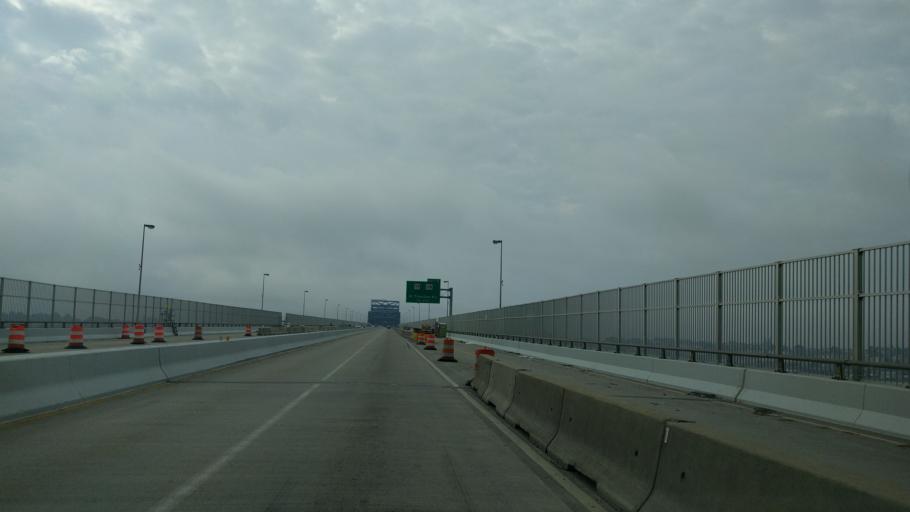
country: US
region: Massachusetts
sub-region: Bristol County
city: Fall River
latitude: 41.7113
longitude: -71.1742
